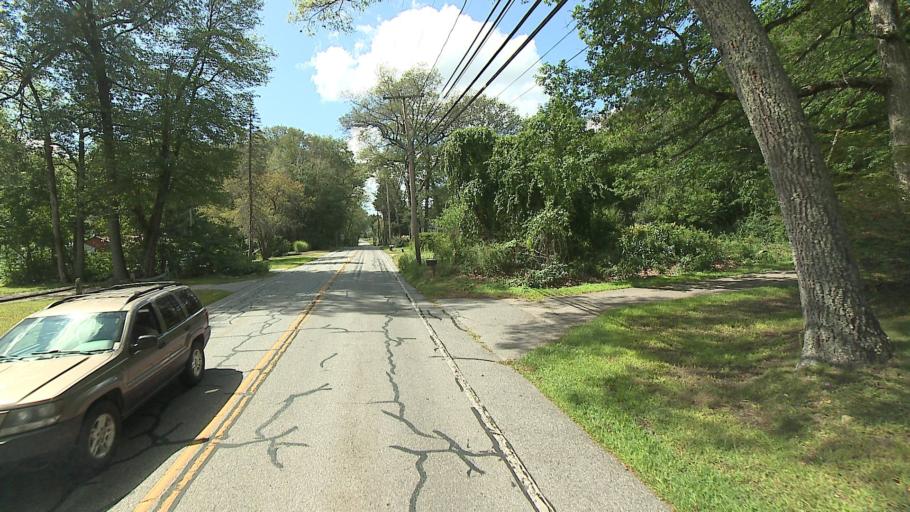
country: US
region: Connecticut
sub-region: Windham County
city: Putnam
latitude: 41.9054
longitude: -71.9210
